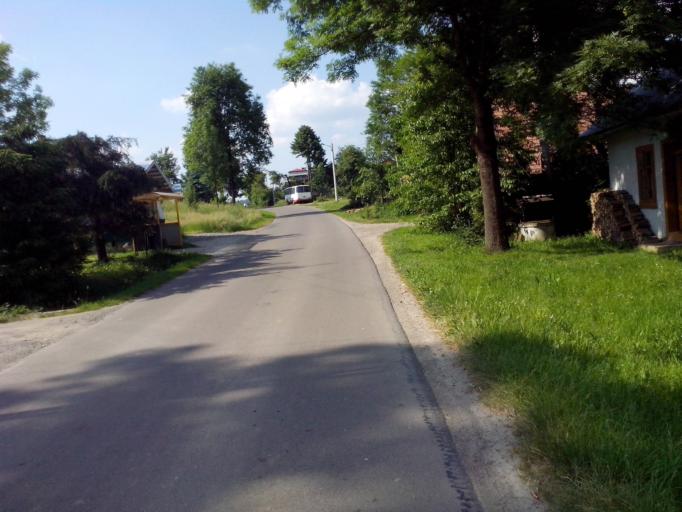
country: PL
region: Subcarpathian Voivodeship
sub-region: Powiat brzozowski
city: Blizne
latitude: 49.7430
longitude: 21.9745
